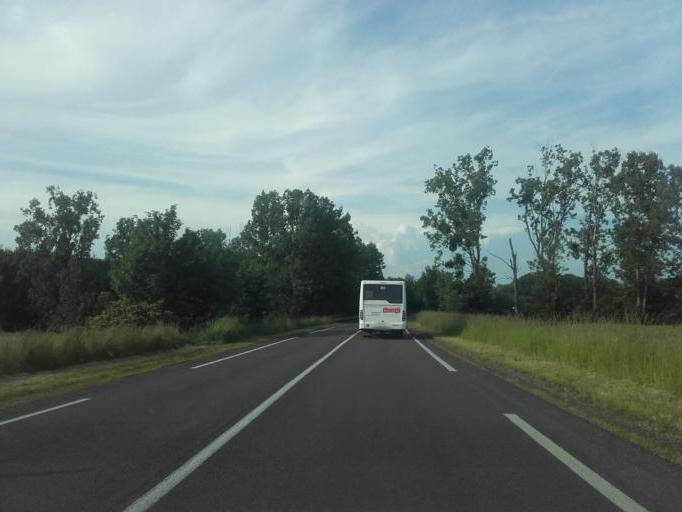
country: FR
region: Bourgogne
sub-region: Departement de Saone-et-Loire
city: Chagny
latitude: 46.9092
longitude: 4.7122
